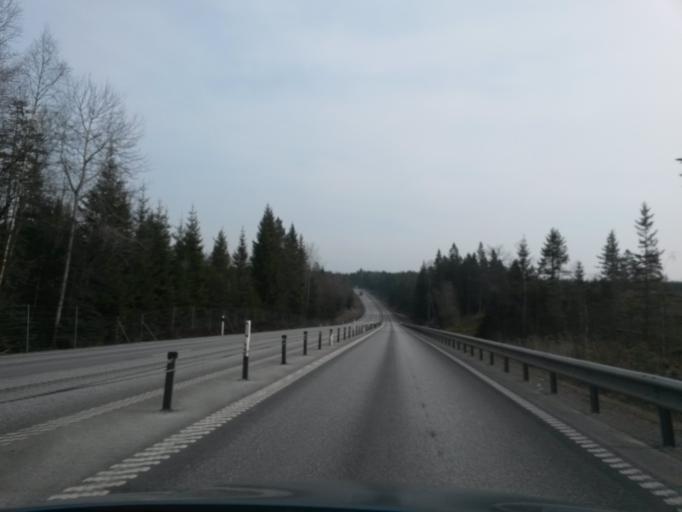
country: SE
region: OErebro
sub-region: Laxa Kommun
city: Laxa
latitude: 58.9509
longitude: 14.4914
